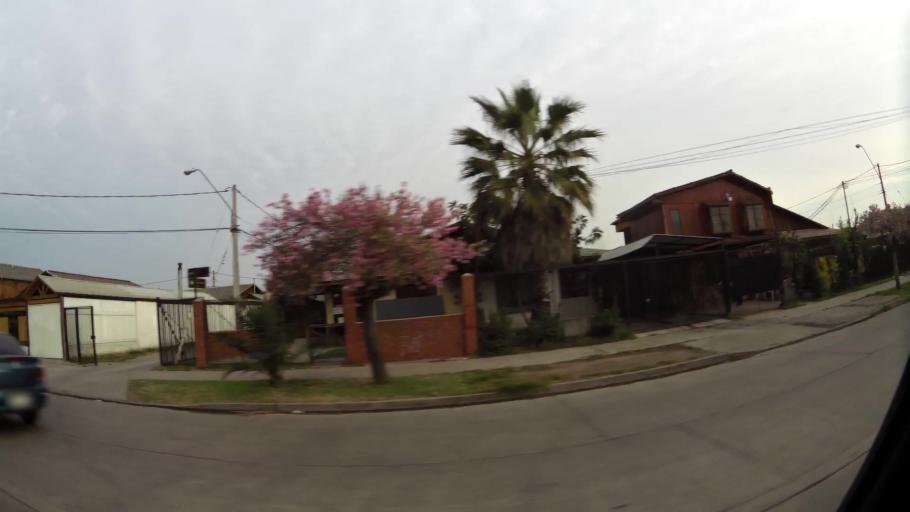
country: CL
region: Santiago Metropolitan
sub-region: Provincia de Santiago
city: Lo Prado
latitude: -33.5221
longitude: -70.7889
